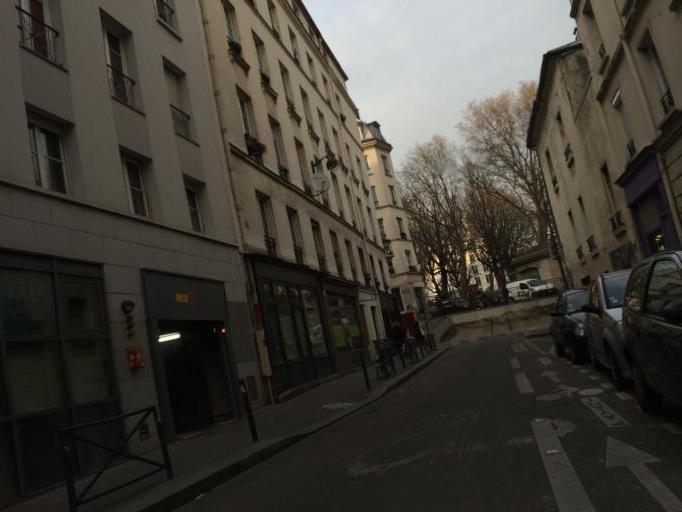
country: FR
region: Ile-de-France
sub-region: Paris
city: Paris
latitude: 48.8727
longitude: 2.3635
